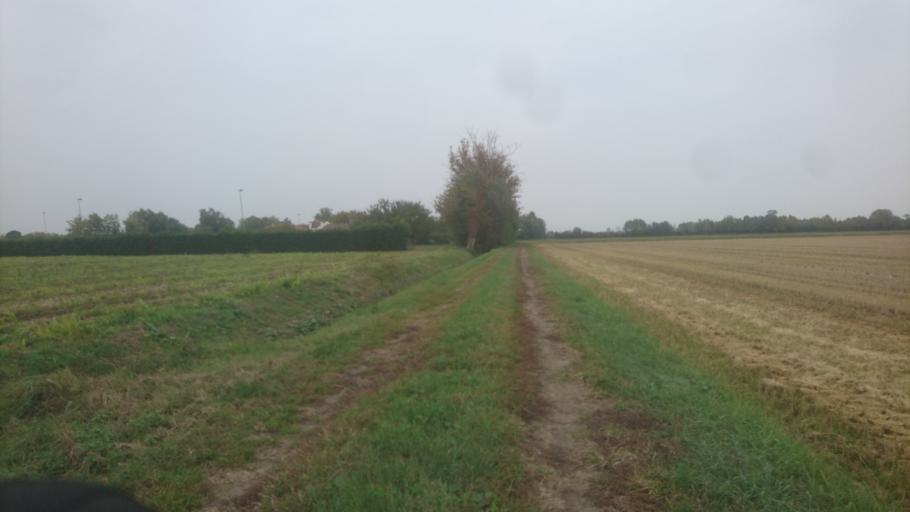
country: IT
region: Veneto
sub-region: Provincia di Vicenza
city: Grumolo delle Abbadesse
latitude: 45.5512
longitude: 11.6708
